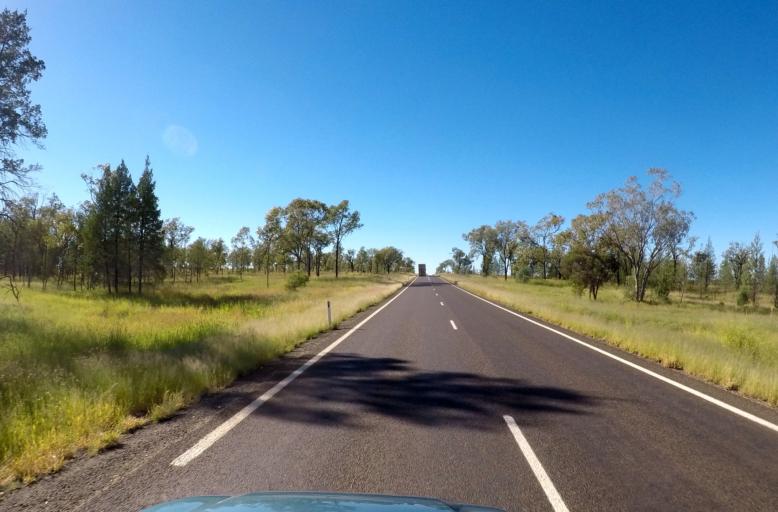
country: AU
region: Queensland
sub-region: Maranoa
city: Roma
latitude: -26.3897
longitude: 148.7821
